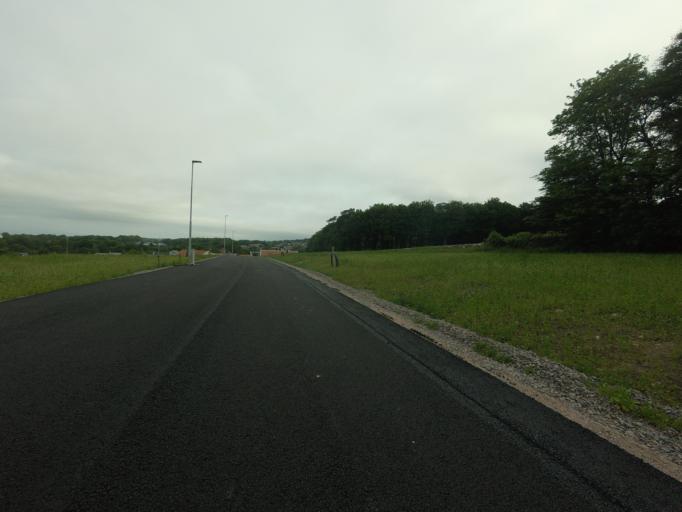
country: SE
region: Skane
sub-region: Bastads Kommun
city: Forslov
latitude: 56.3491
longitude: 12.8258
